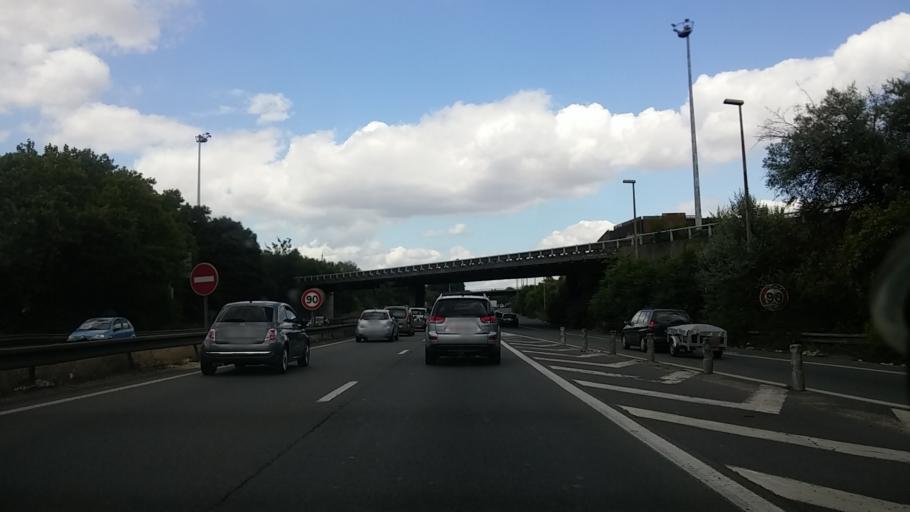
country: FR
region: Ile-de-France
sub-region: Departement de Seine-Saint-Denis
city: Le Blanc-Mesnil
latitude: 48.9582
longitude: 2.4734
